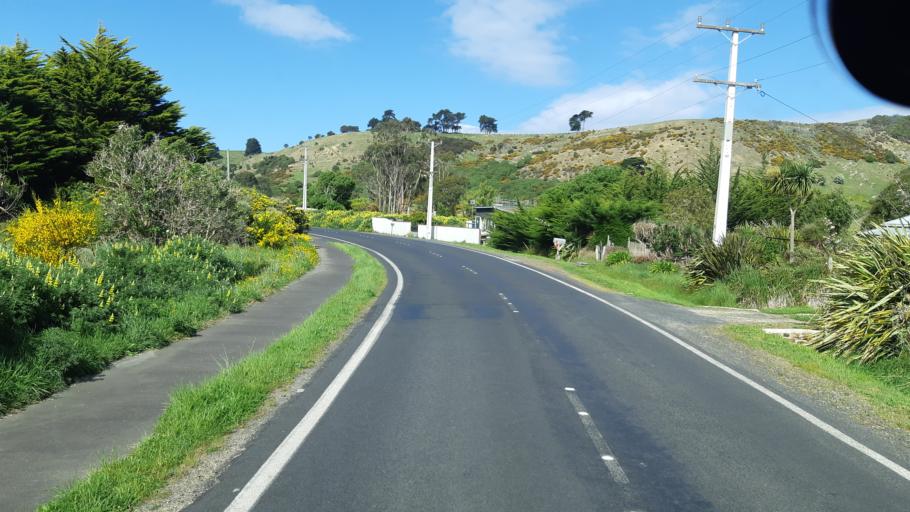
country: NZ
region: Otago
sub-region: Dunedin City
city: Portobello
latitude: -45.7985
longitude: 170.7203
